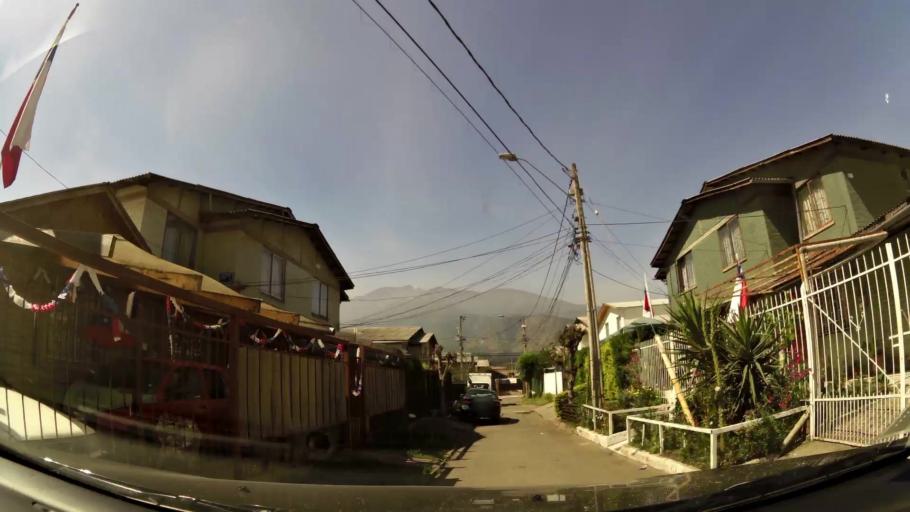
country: CL
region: Santiago Metropolitan
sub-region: Provincia de Cordillera
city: Puente Alto
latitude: -33.5645
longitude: -70.5635
